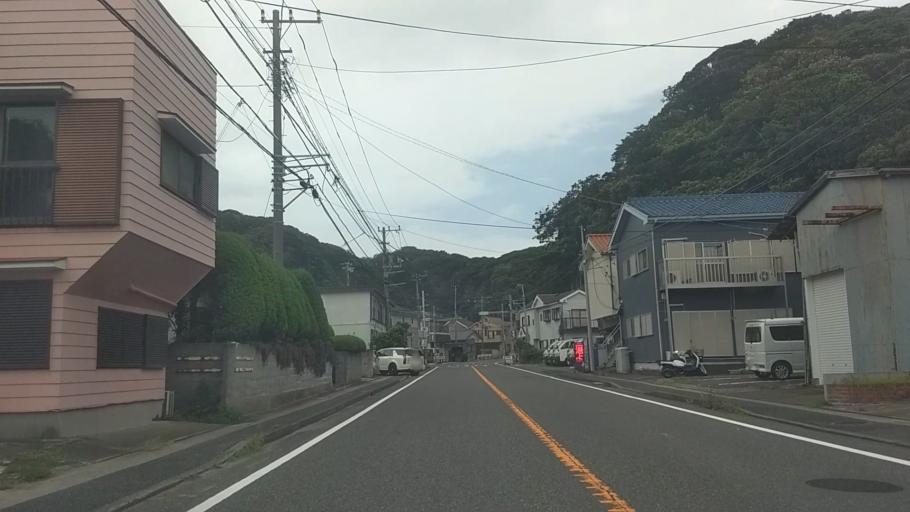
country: JP
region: Kanagawa
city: Yokosuka
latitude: 35.2522
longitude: 139.7369
